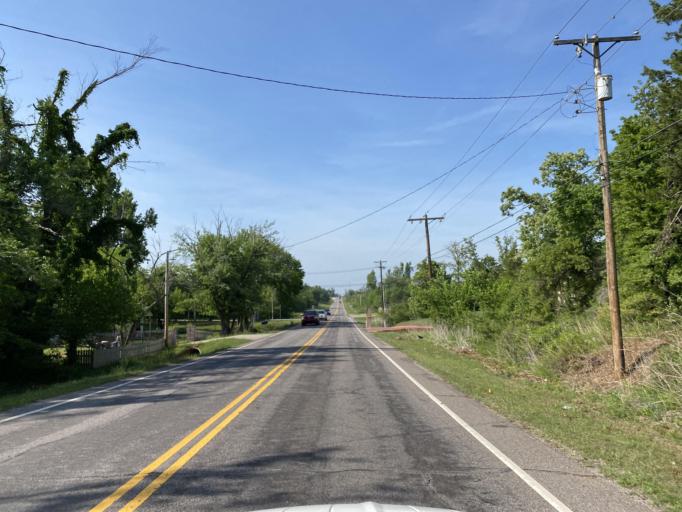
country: US
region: Oklahoma
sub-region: Oklahoma County
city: Nicoma Park
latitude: 35.4418
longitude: -97.3357
